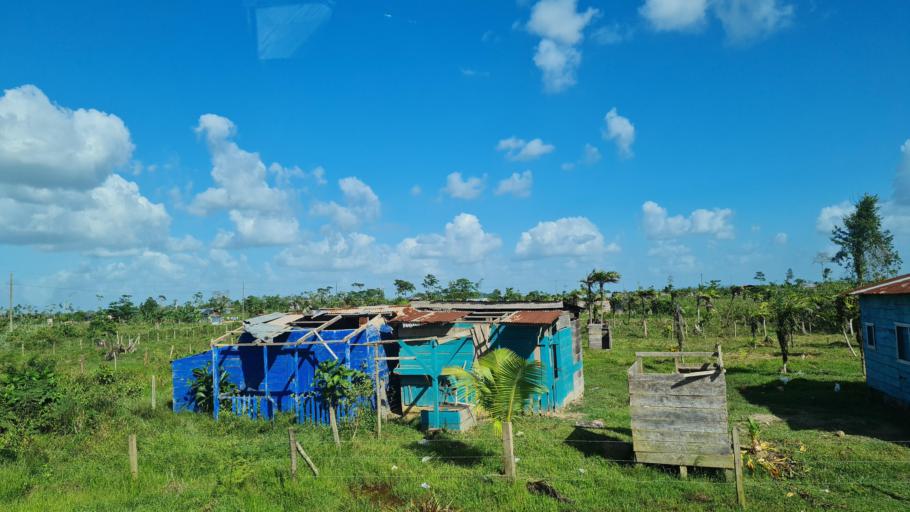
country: NI
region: Atlantico Norte (RAAN)
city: Bonanza
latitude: 13.9833
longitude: -84.1881
